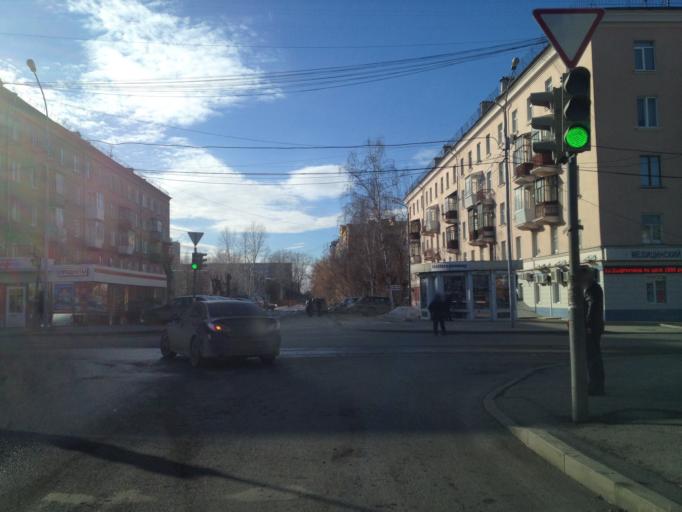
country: RU
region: Sverdlovsk
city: Yekaterinburg
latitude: 56.8333
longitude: 60.5529
